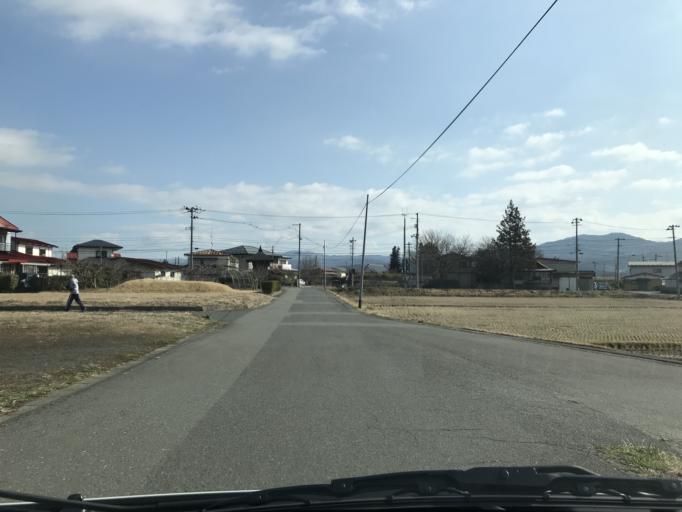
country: JP
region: Iwate
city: Mizusawa
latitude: 39.0356
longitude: 141.1231
